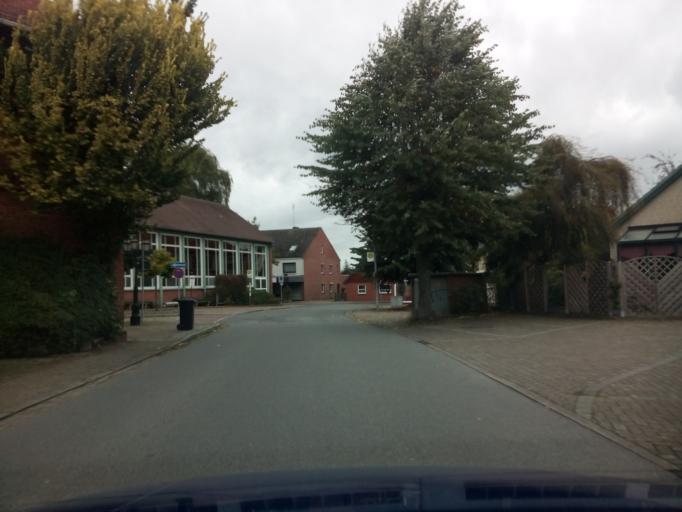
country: DE
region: Lower Saxony
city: Beverstedt
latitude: 53.4349
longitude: 8.8224
